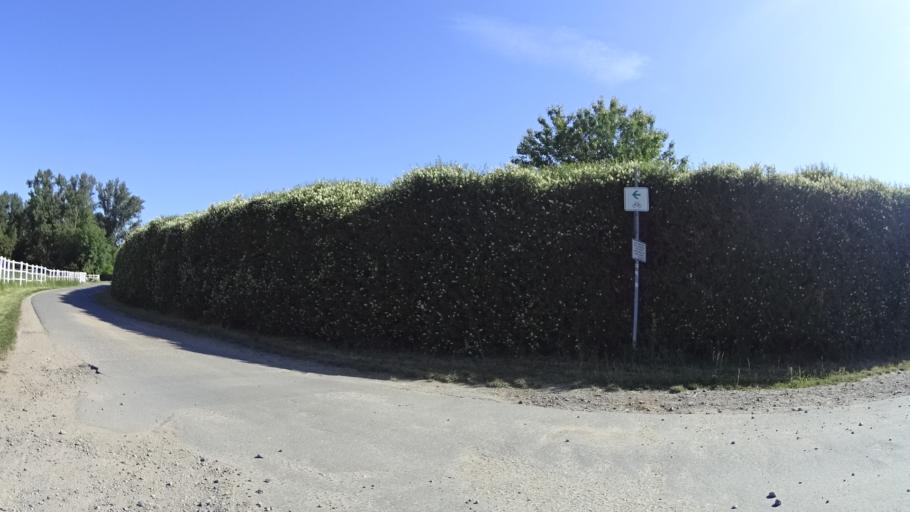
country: DE
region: Hesse
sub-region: Regierungsbezirk Darmstadt
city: Alsbach-Hahnlein
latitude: 49.7502
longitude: 8.5878
